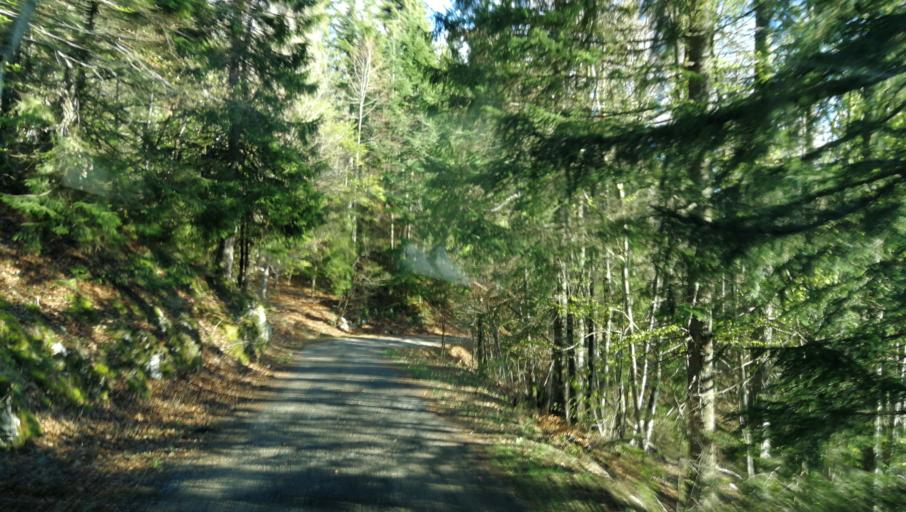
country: FR
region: Rhone-Alpes
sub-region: Departement de l'Ain
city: Chatillon-en-Michaille
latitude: 46.2621
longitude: 5.7978
